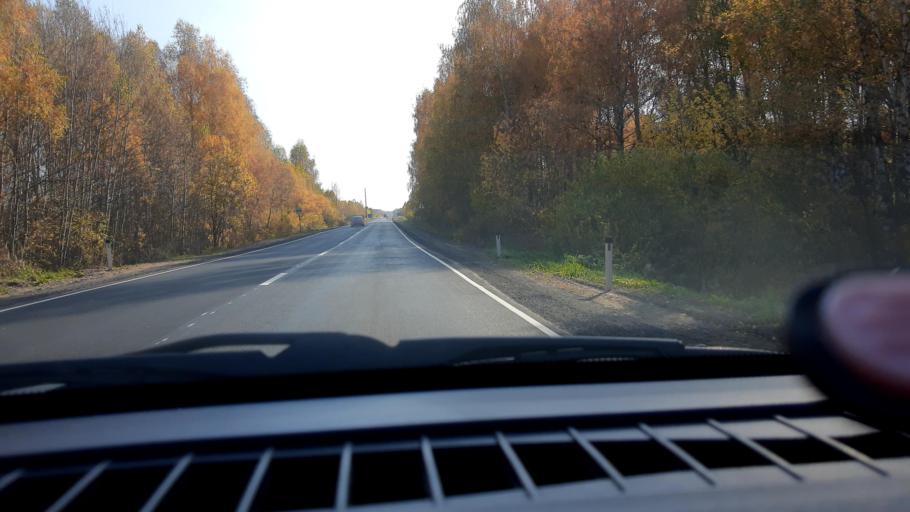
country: RU
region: Nizjnij Novgorod
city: Novaya Balakhna
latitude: 56.5899
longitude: 43.6638
